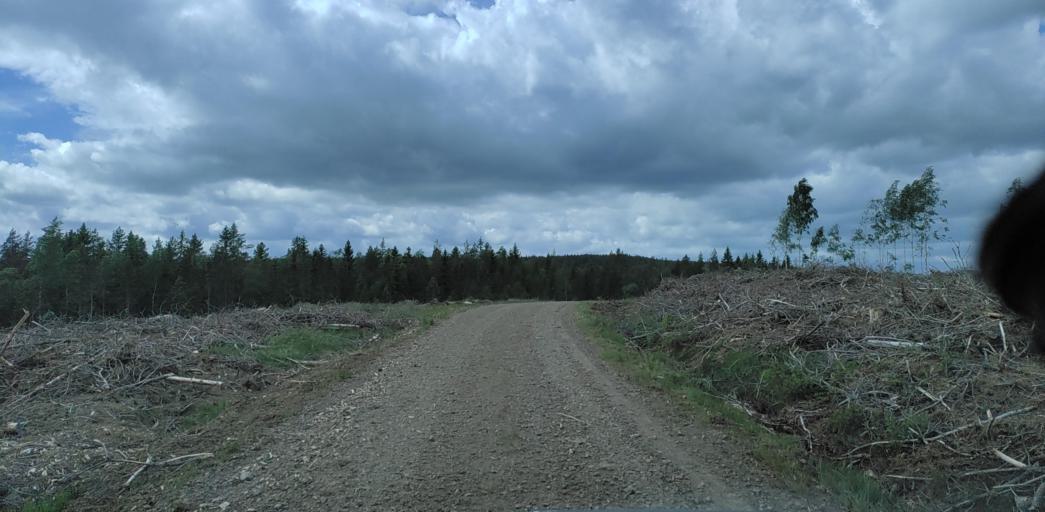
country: SE
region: Vaermland
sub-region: Munkfors Kommun
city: Munkfors
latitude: 59.9496
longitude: 13.4165
